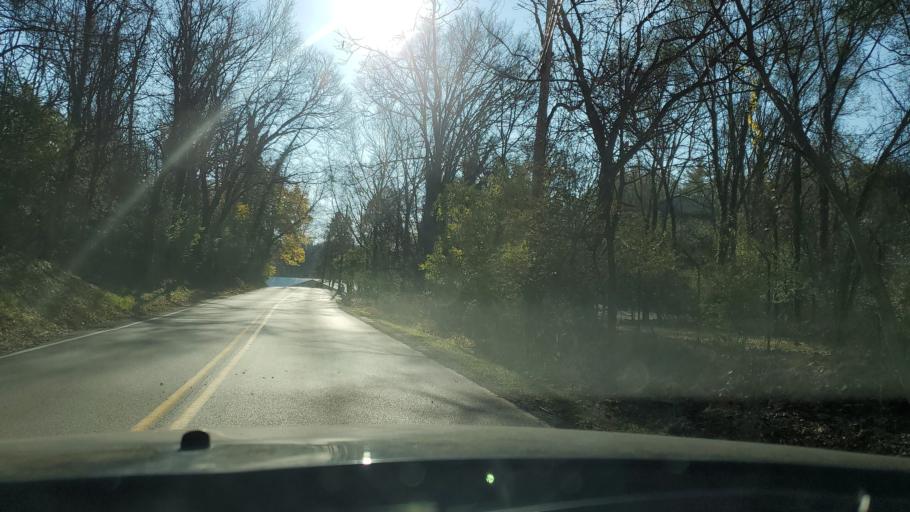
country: US
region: Pennsylvania
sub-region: Cumberland County
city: Mechanicsburg
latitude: 40.1659
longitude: -76.9840
